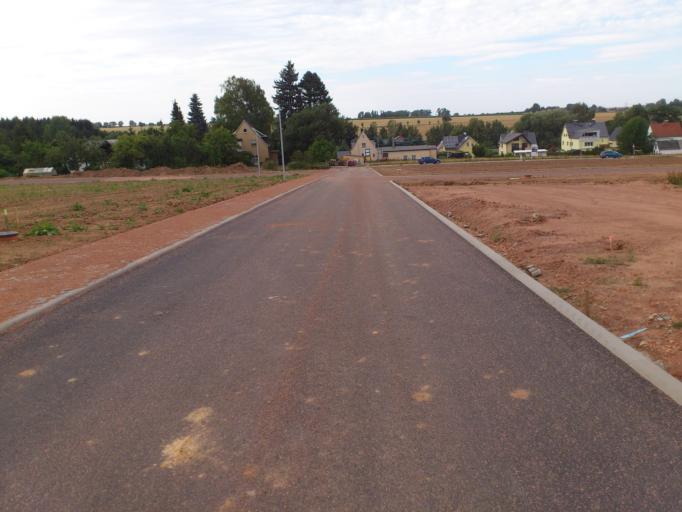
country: DE
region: Saxony
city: Neukirchen
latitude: 50.7773
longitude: 12.8455
